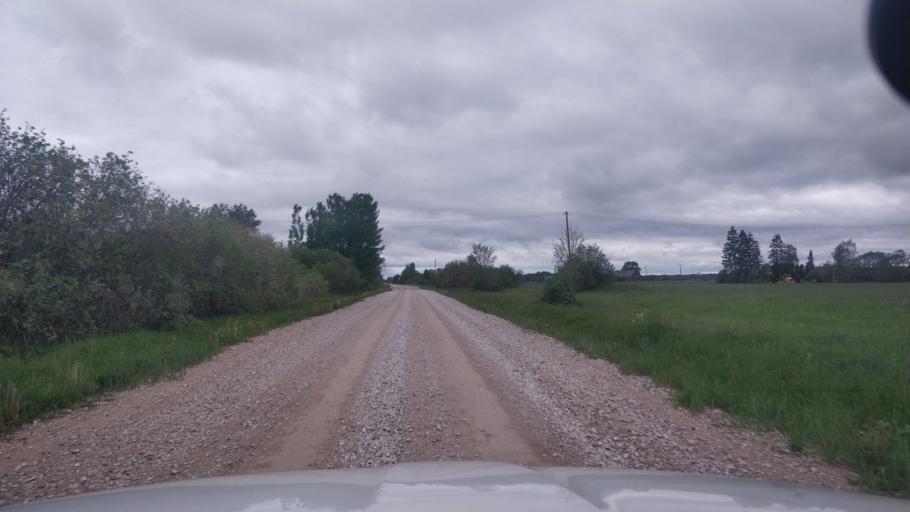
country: EE
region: Raplamaa
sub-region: Maerjamaa vald
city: Marjamaa
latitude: 58.7547
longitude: 24.2234
